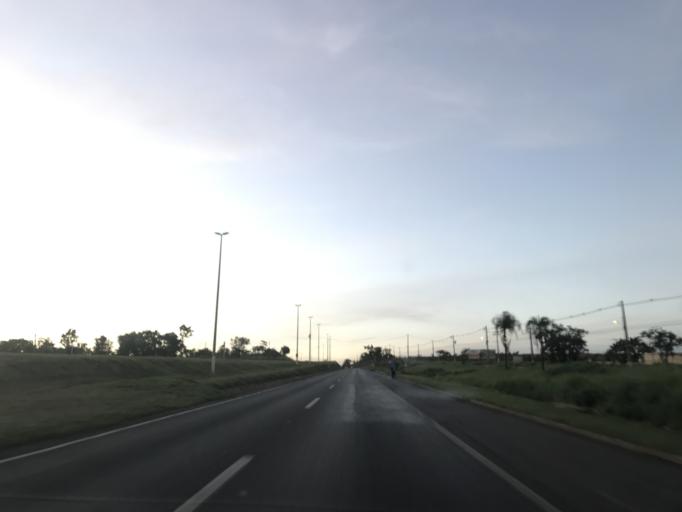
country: BR
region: Goias
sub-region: Luziania
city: Luziania
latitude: -16.1832
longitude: -47.9288
